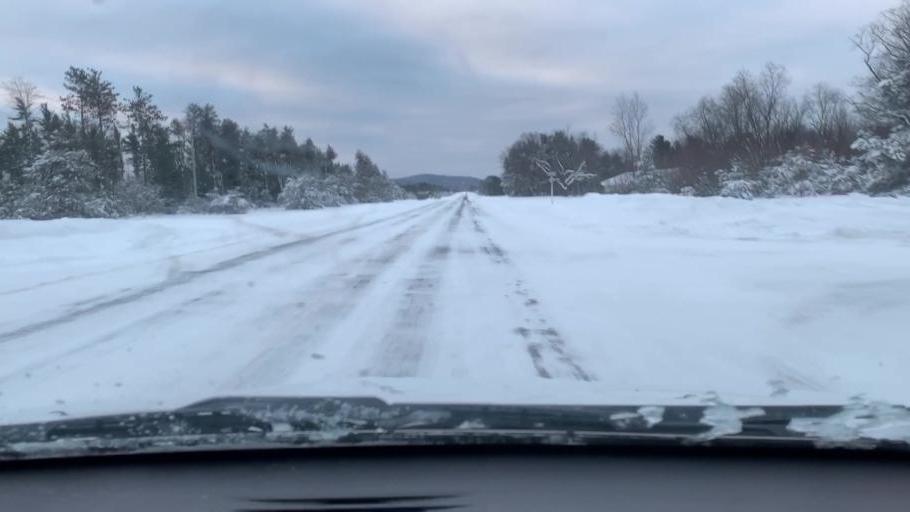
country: US
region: Michigan
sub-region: Antrim County
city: Mancelona
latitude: 44.9315
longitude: -85.0509
